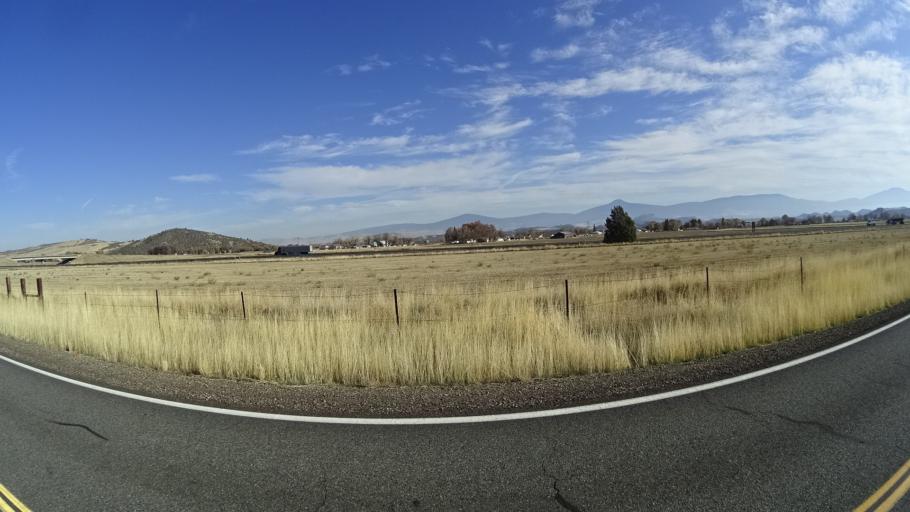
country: US
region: California
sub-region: Siskiyou County
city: Montague
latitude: 41.6428
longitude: -122.5352
